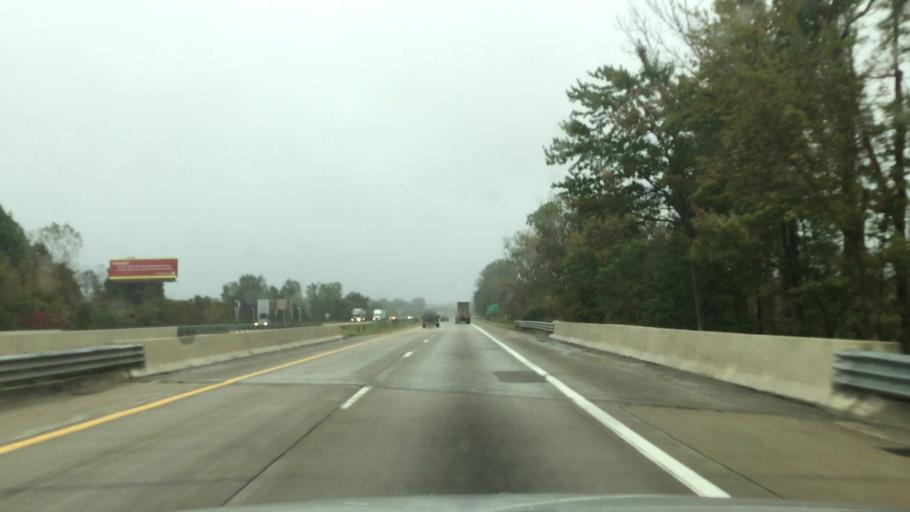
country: US
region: Michigan
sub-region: Van Buren County
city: Paw Paw
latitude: 42.2056
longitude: -85.9022
